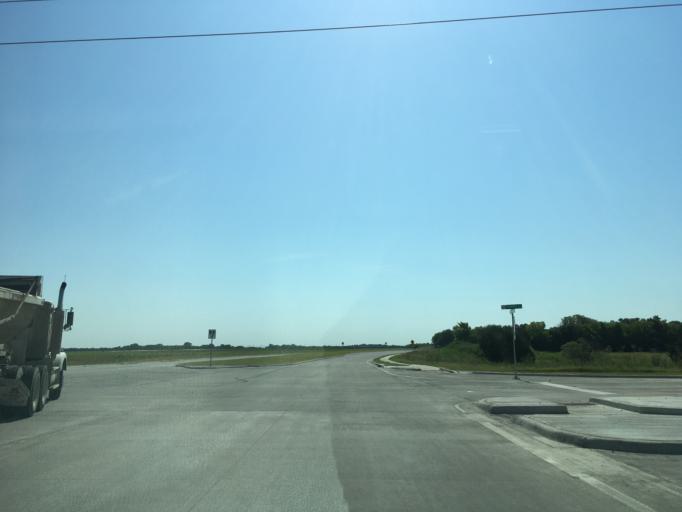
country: US
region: Texas
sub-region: Collin County
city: Fairview
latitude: 33.1658
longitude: -96.5992
